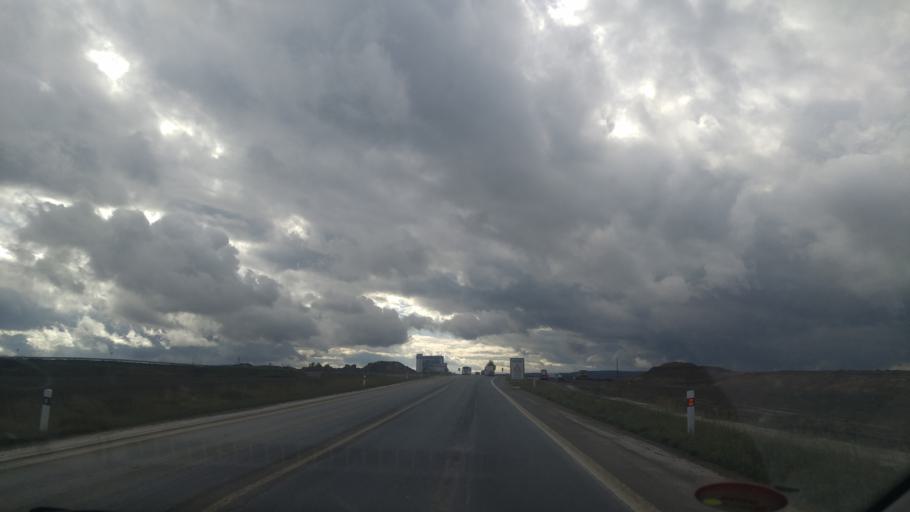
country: CZ
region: Jihocesky
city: Dolni Bukovsko
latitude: 49.1557
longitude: 14.6364
